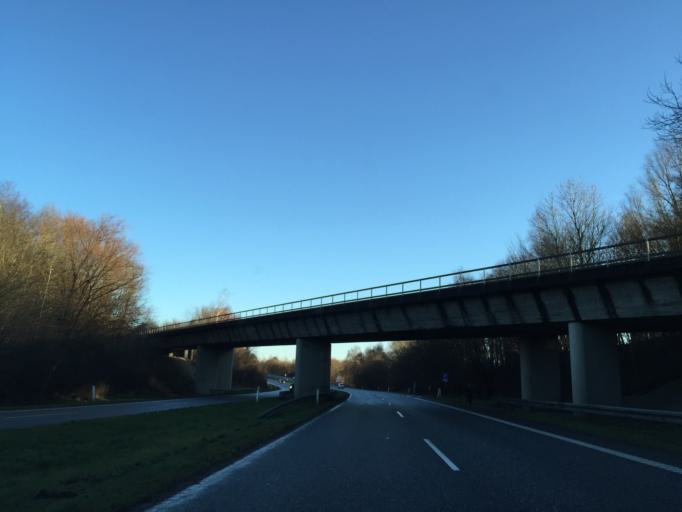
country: DK
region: Central Jutland
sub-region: Skanderborg Kommune
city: Skanderborg
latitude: 56.0427
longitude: 9.9125
